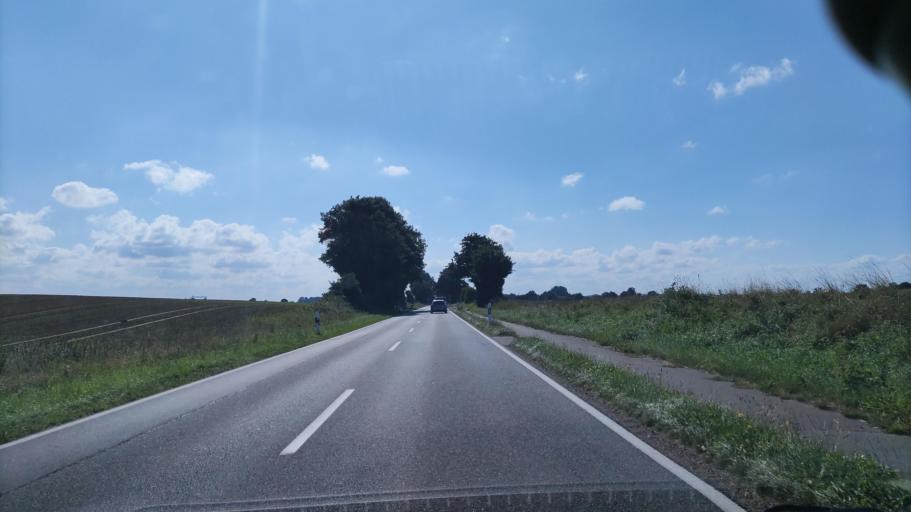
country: DE
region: Schleswig-Holstein
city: Osterby
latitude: 54.4566
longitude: 9.7675
